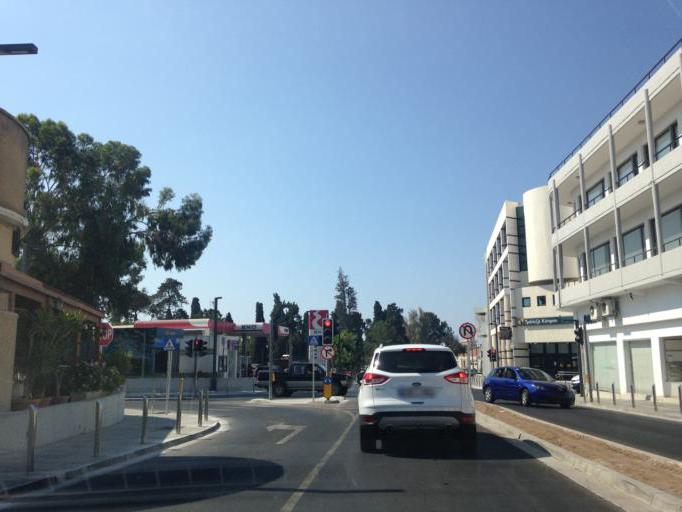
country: CY
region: Pafos
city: Paphos
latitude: 34.7773
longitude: 32.4235
